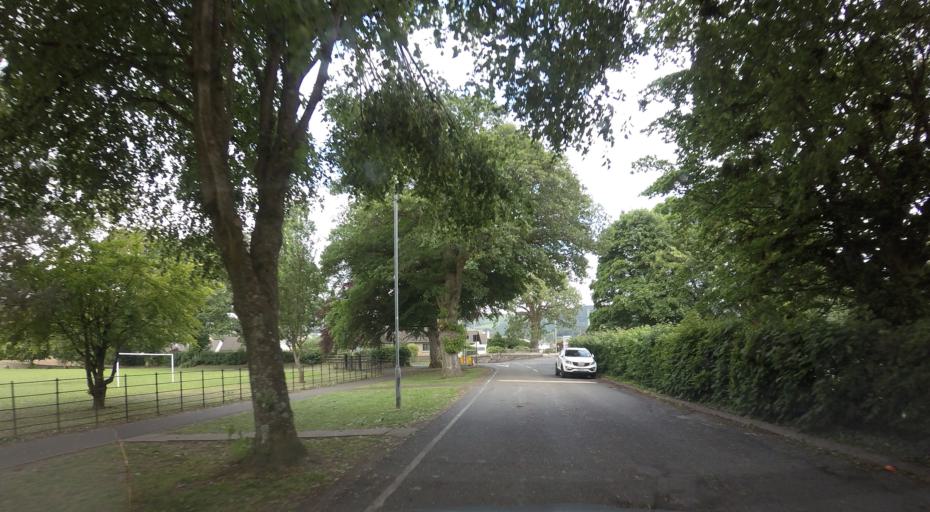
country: GB
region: England
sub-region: Cumbria
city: Keswick
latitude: 54.6071
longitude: -3.1490
